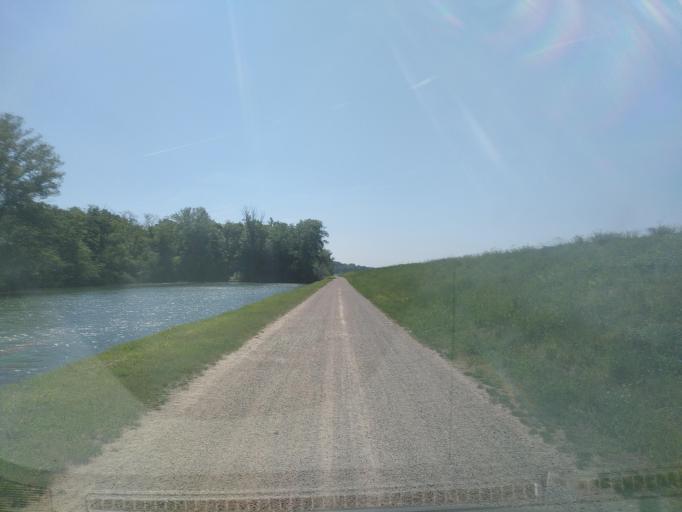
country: DE
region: Baden-Wuerttemberg
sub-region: Freiburg Region
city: Breisach am Rhein
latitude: 48.0668
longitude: 7.5736
